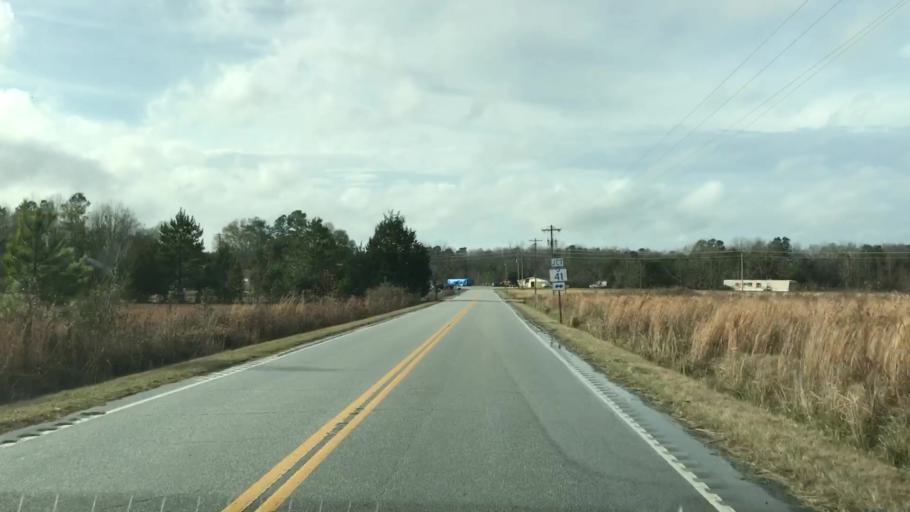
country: US
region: South Carolina
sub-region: Williamsburg County
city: Andrews
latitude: 33.5025
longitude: -79.5220
